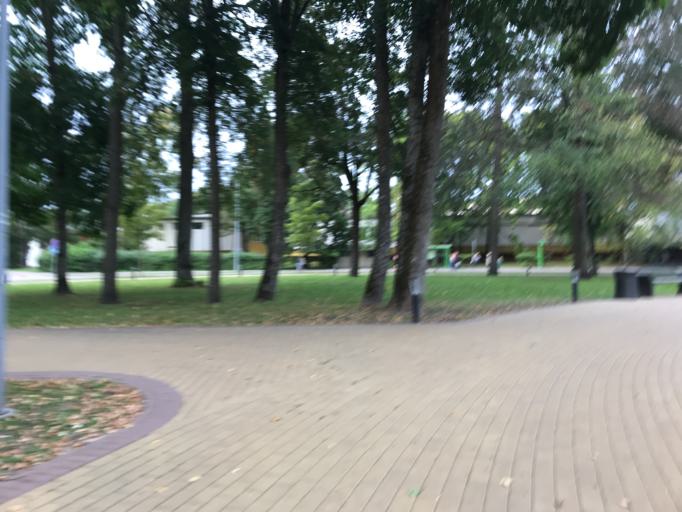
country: LT
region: Alytaus apskritis
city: Druskininkai
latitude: 54.0212
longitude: 23.9710
